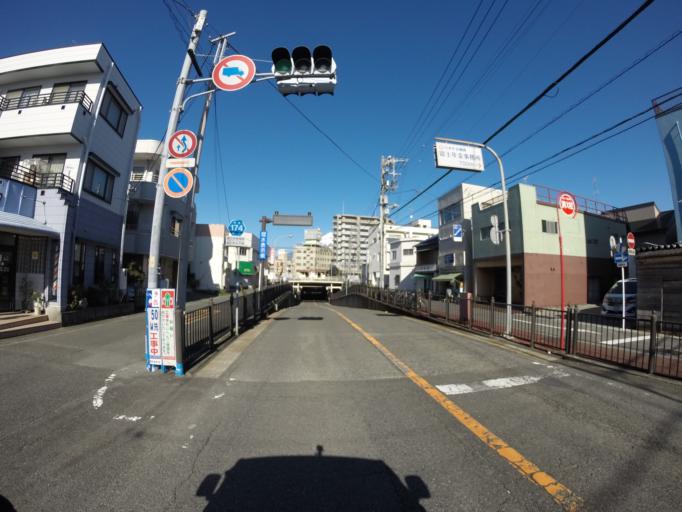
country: JP
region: Shizuoka
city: Fuji
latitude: 35.1505
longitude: 138.6493
